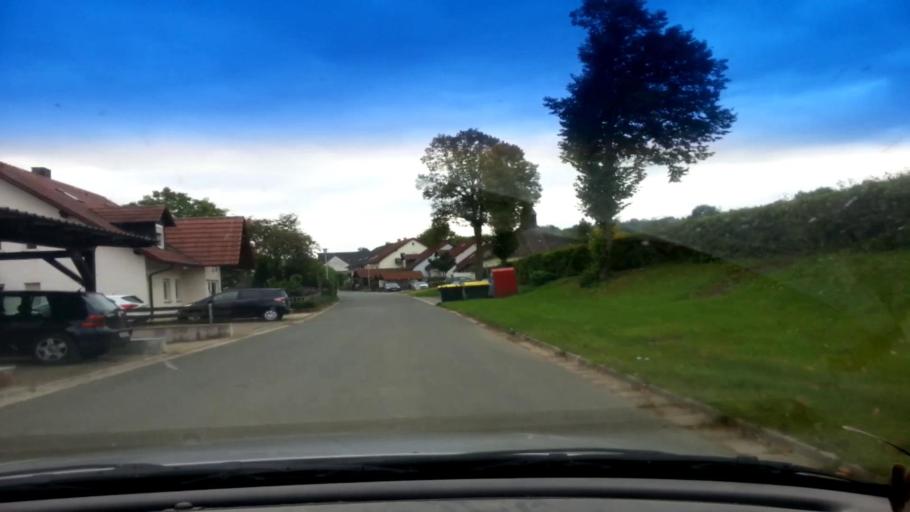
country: DE
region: Bavaria
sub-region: Upper Franconia
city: Zapfendorf
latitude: 50.0041
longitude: 10.9387
